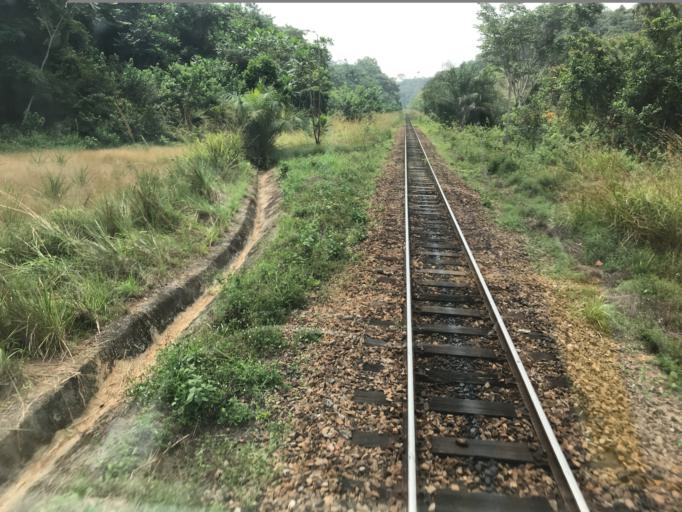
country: CM
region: Centre
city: Eseka
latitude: 3.5792
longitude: 10.8927
